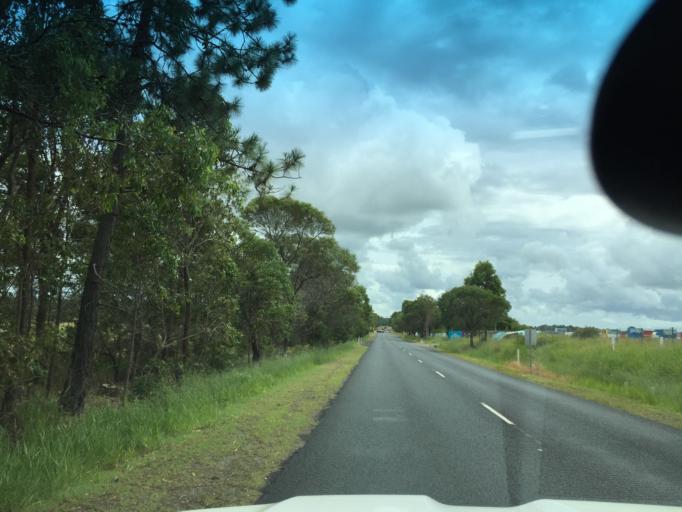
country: AU
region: Queensland
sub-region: Moreton Bay
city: Morayfield
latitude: -27.1136
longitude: 152.9799
